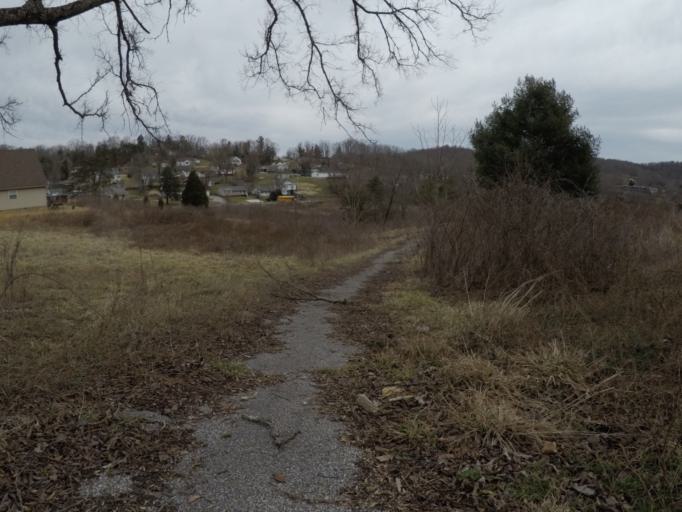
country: US
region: Ohio
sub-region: Lawrence County
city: Burlington
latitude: 38.3831
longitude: -82.5159
